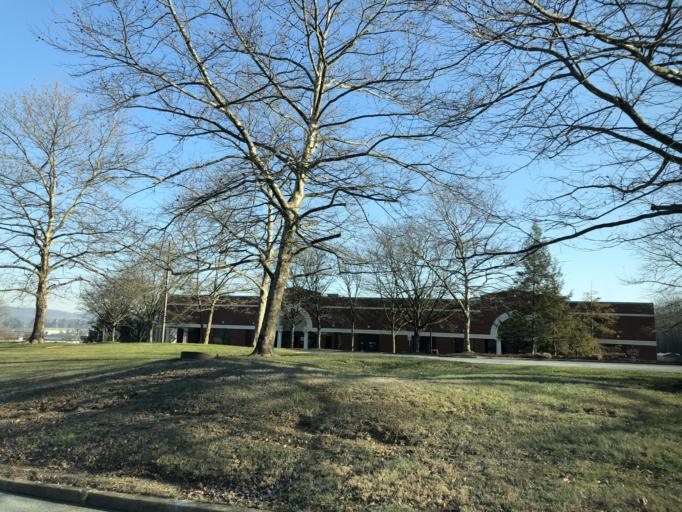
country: US
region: Pennsylvania
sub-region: Chester County
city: Downingtown
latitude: 40.0012
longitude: -75.6903
